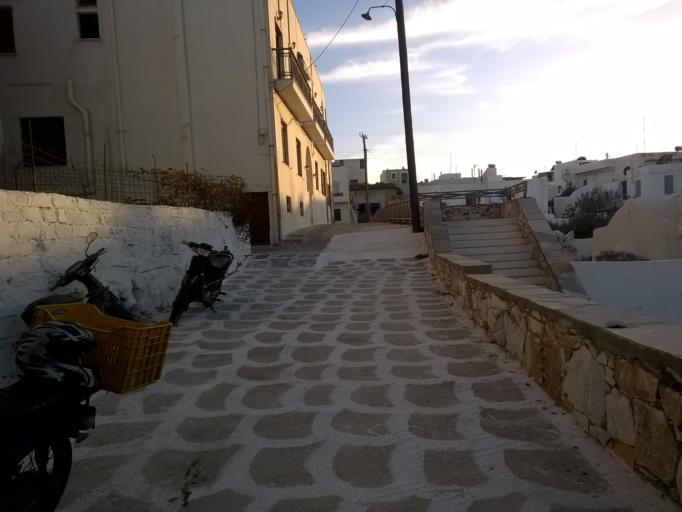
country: GR
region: South Aegean
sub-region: Nomos Kykladon
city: Naxos
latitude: 37.1053
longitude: 25.3783
